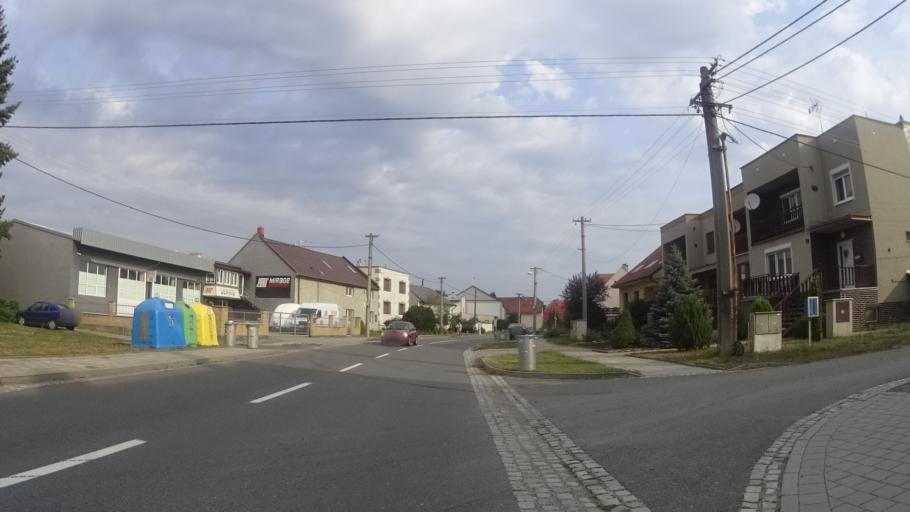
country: CZ
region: Zlin
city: Chropyne
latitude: 49.3375
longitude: 17.3823
